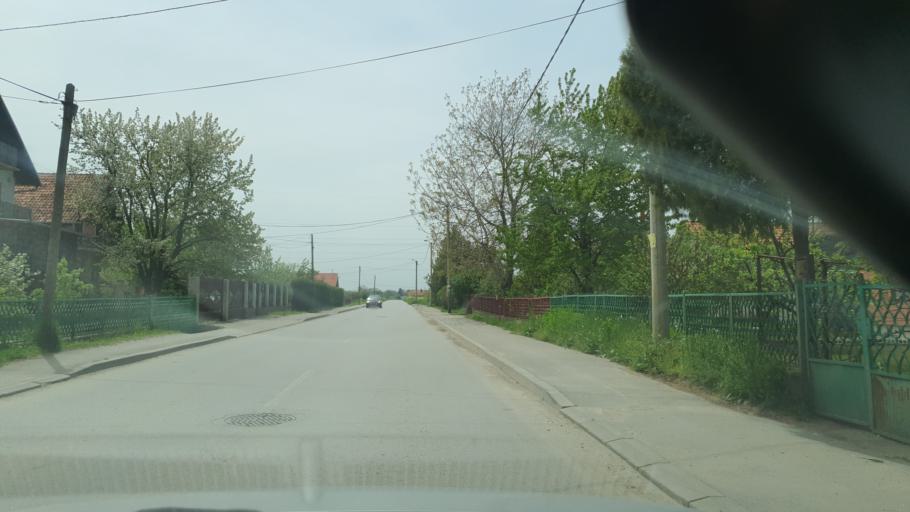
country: RS
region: Central Serbia
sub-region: Branicevski Okrug
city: Pozarevac
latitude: 44.7021
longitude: 21.1591
